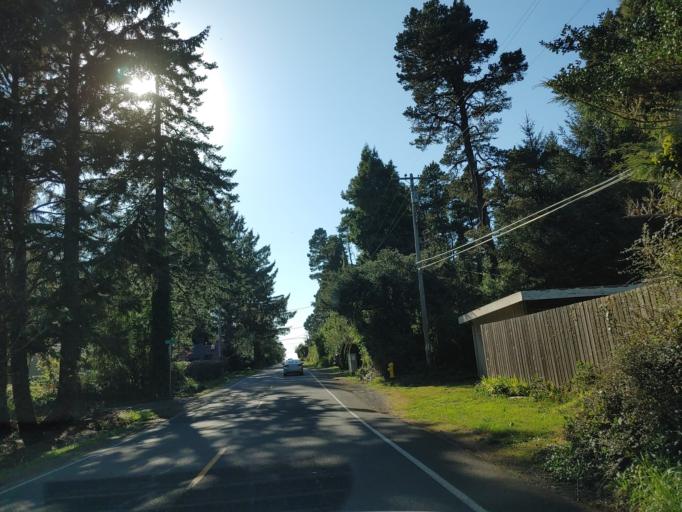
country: US
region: Oregon
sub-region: Lincoln County
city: Depoe Bay
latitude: 44.7471
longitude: -124.0570
